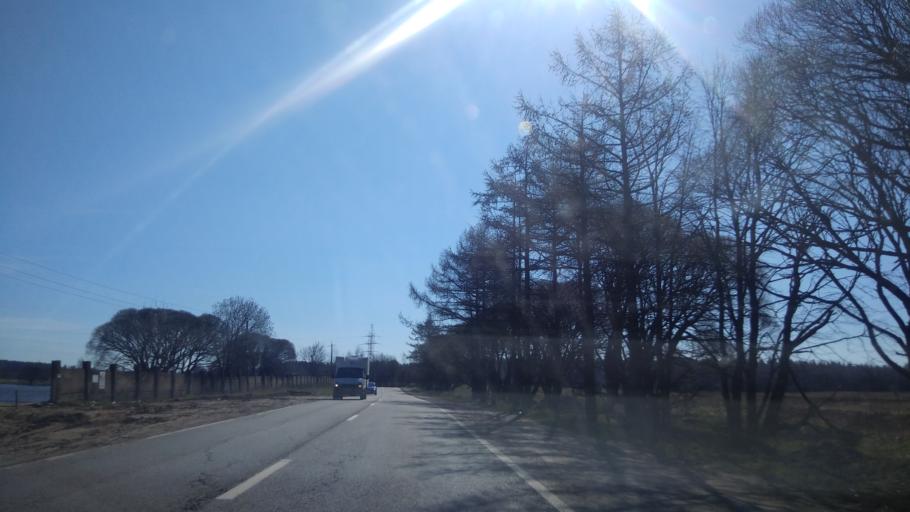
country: RU
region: Moskovskaya
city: Pravdinskiy
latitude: 56.0444
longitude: 37.8857
